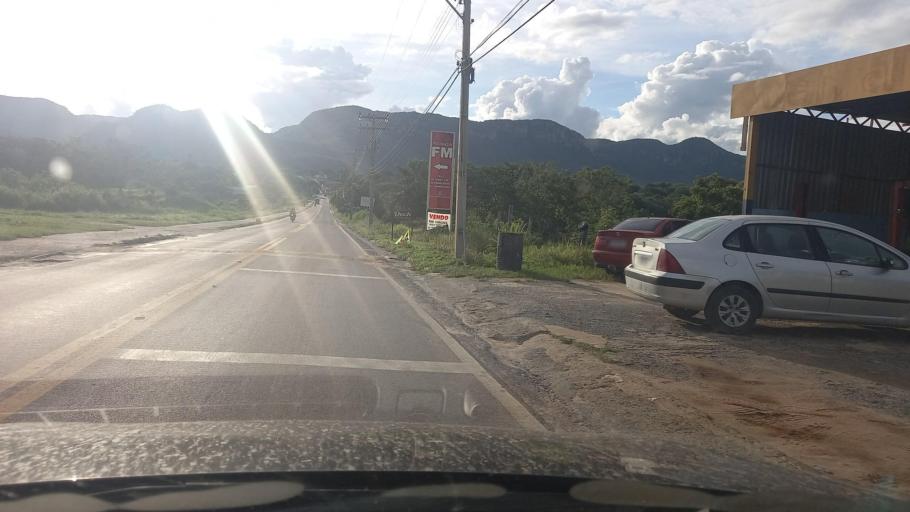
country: BR
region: Goias
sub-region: Cavalcante
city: Cavalcante
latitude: -13.7967
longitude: -47.4520
